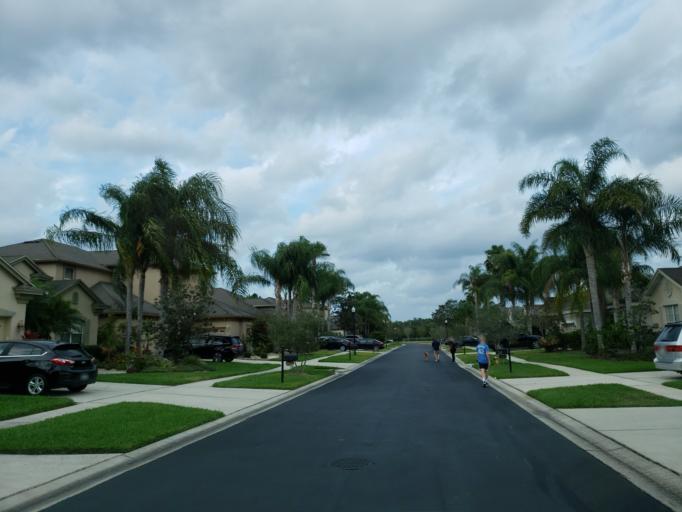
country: US
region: Florida
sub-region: Pasco County
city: Wesley Chapel
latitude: 28.2077
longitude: -82.3621
